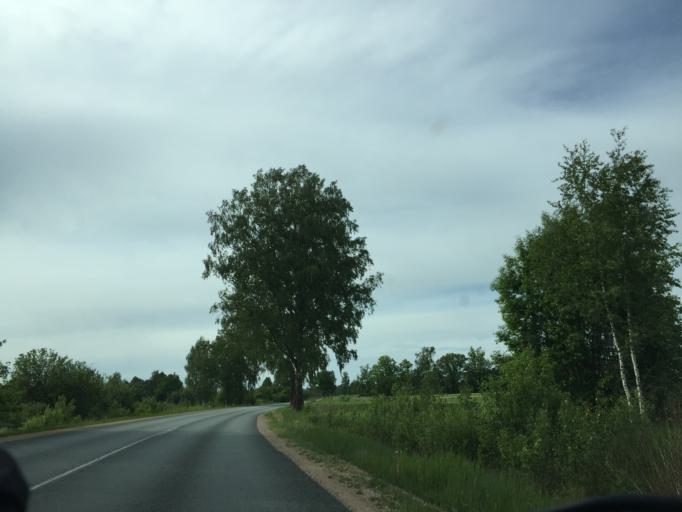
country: LV
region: Beverina
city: Murmuiza
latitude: 57.4525
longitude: 25.4243
